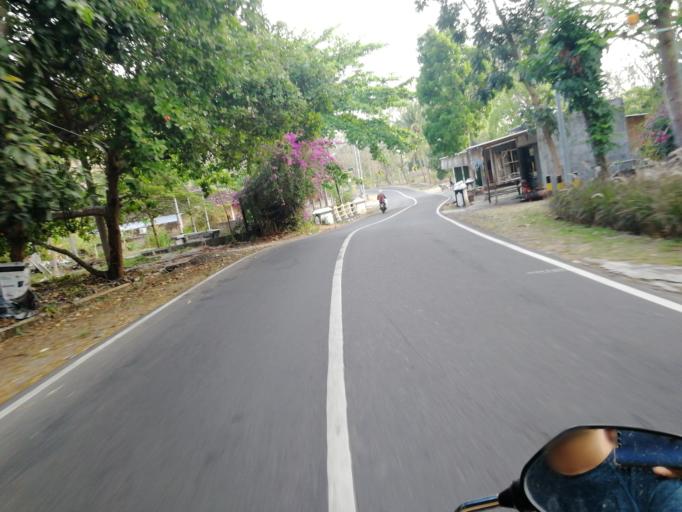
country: ID
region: West Nusa Tenggara
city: Karangsubagan
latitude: -8.4583
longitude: 116.0387
